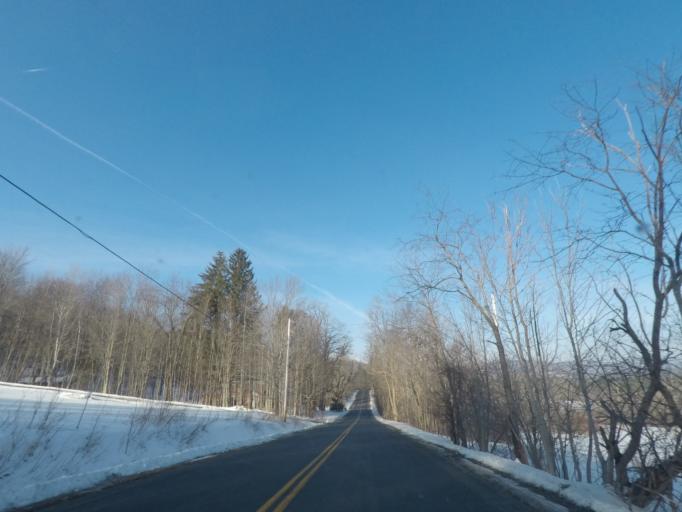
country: US
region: Massachusetts
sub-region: Berkshire County
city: Richmond
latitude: 42.5084
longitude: -73.3787
